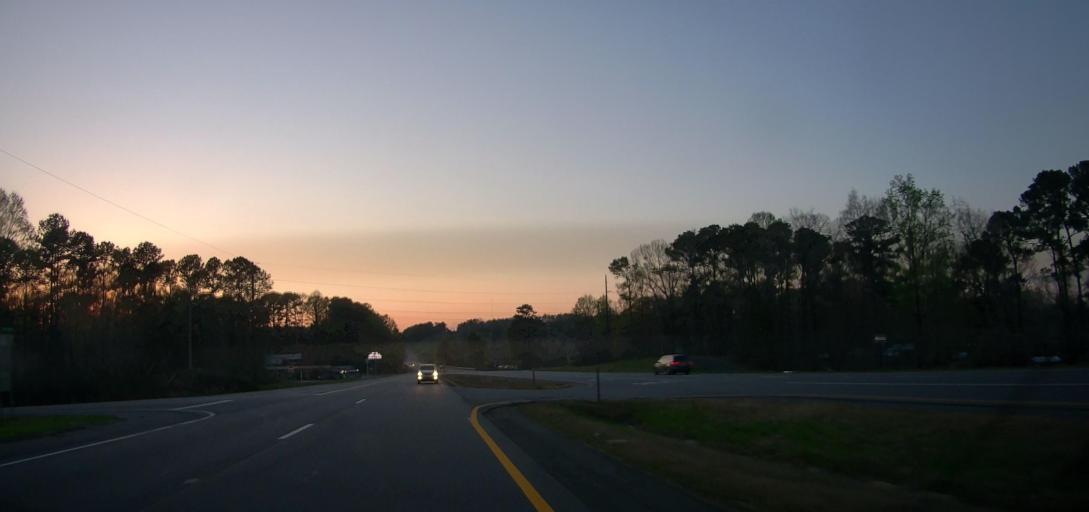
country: US
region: Alabama
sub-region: Tallapoosa County
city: Alexander City
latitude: 32.8971
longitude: -85.8818
